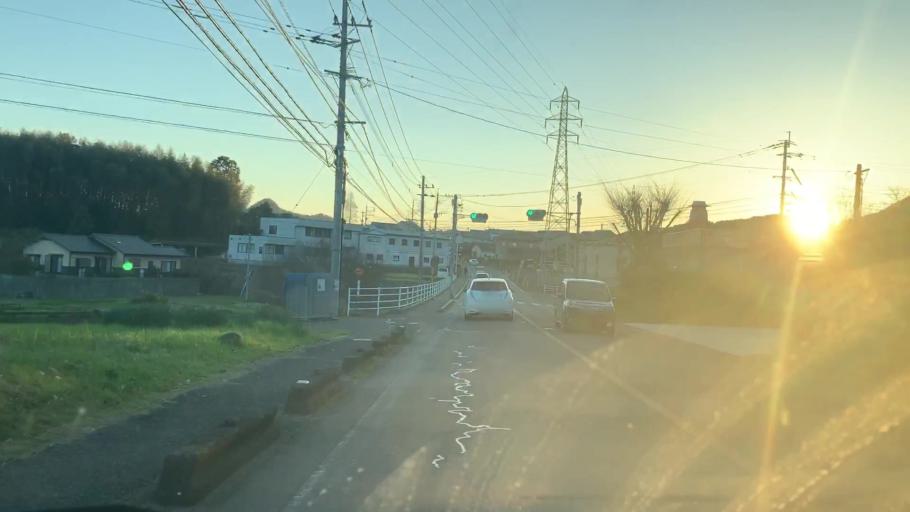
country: JP
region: Saga Prefecture
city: Takeocho-takeo
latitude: 33.2090
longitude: 130.0282
